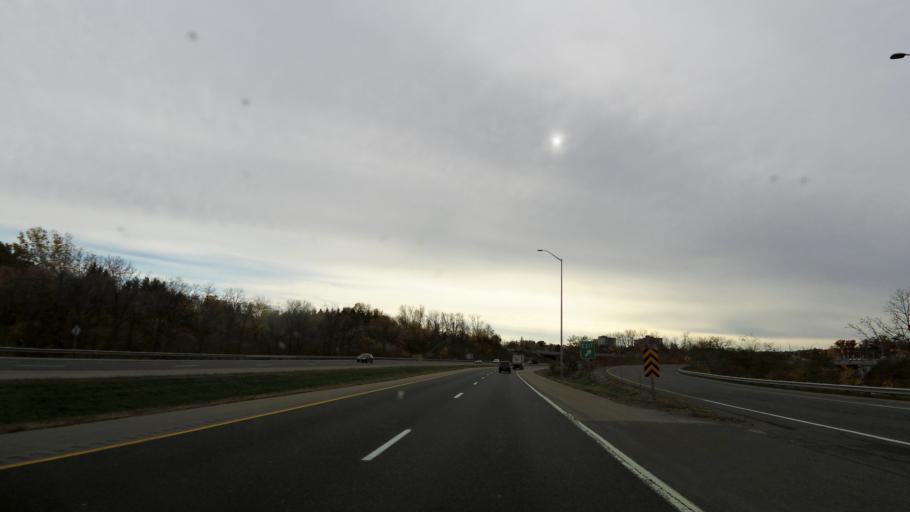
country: CA
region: Ontario
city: Hamilton
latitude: 43.2291
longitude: -79.7878
